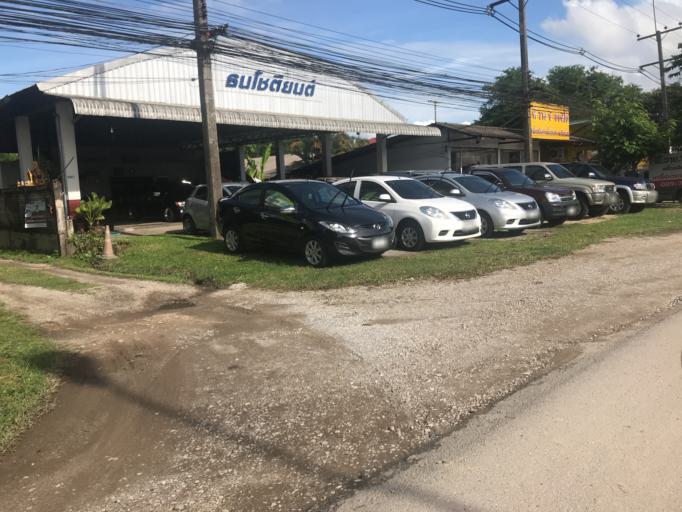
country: TH
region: Chiang Rai
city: Chiang Rai
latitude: 19.9418
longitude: 99.8461
